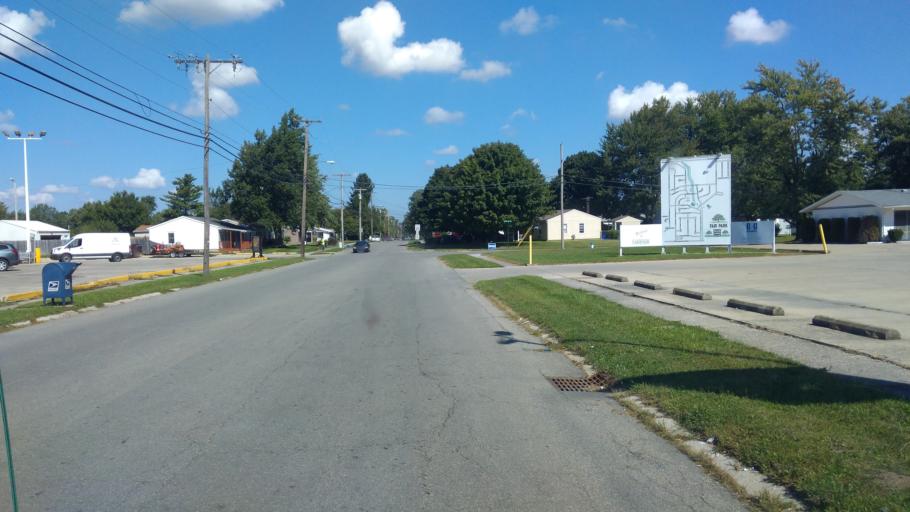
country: US
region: Ohio
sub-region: Marion County
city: Marion
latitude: 40.6008
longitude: -83.1201
